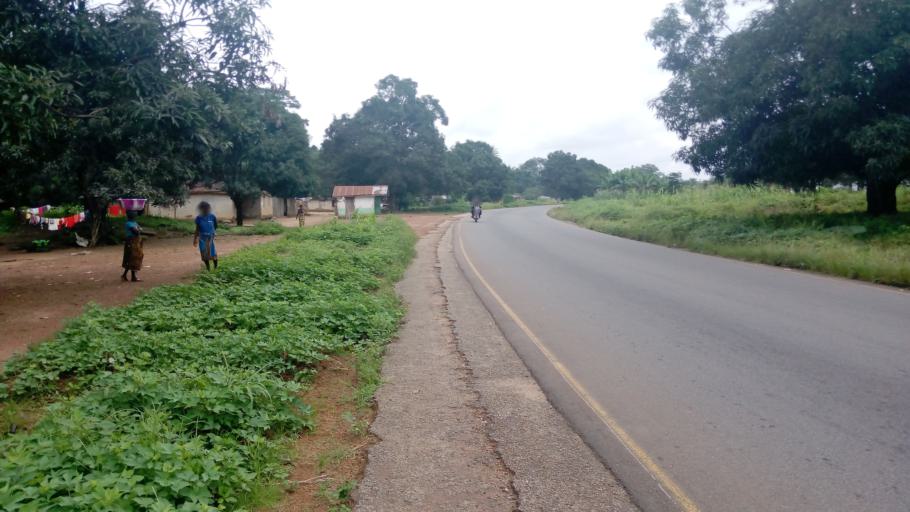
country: SL
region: Northern Province
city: Port Loko
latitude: 8.5061
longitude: -12.7610
